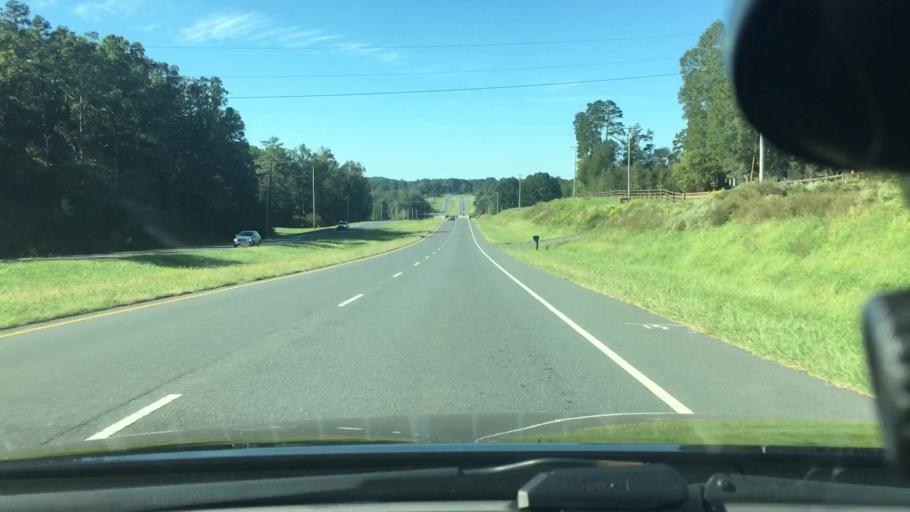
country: US
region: North Carolina
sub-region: Stanly County
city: Oakboro
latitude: 35.2858
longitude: -80.2958
